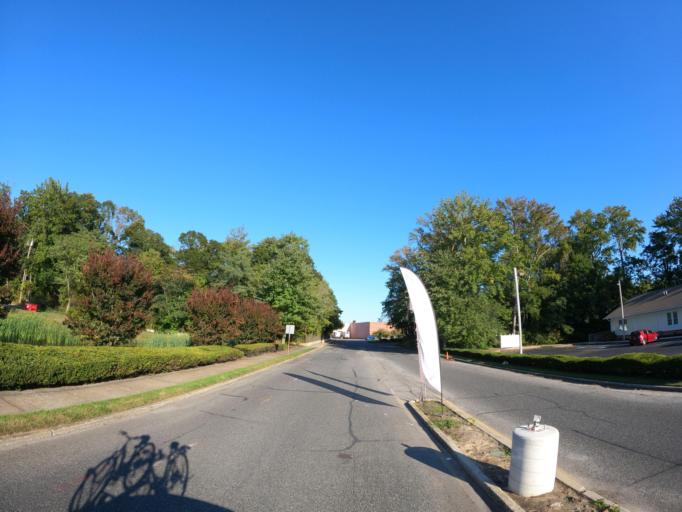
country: US
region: New Jersey
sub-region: Cape May County
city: North Cape May
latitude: 38.9749
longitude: -74.9423
